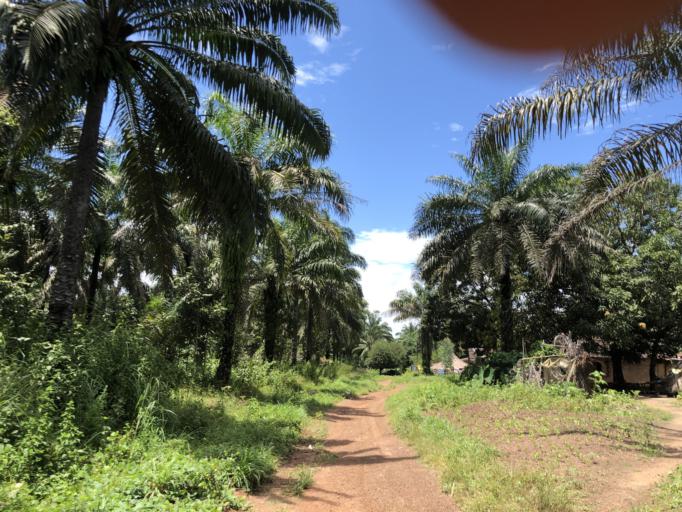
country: SL
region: Northern Province
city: Makeni
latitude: 8.8651
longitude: -12.1288
